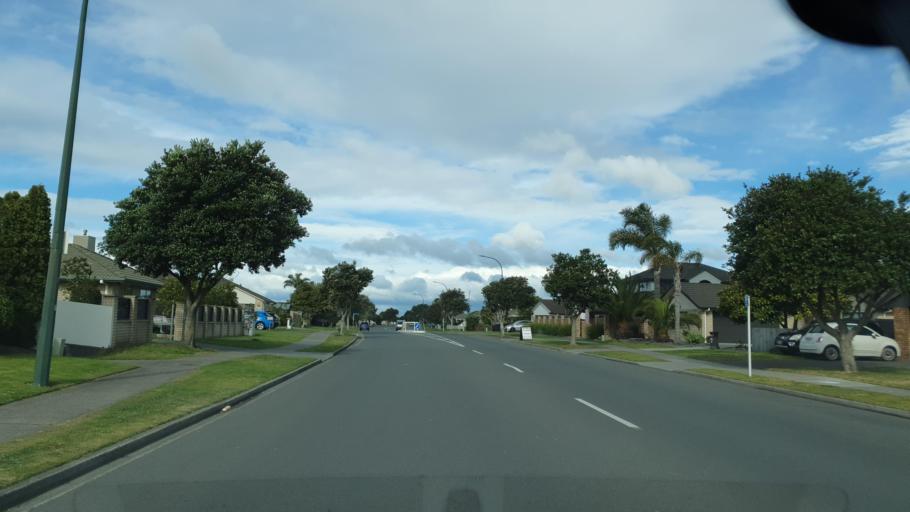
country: NZ
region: Bay of Plenty
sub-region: Tauranga City
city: Tauranga
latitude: -37.6927
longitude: 176.2513
